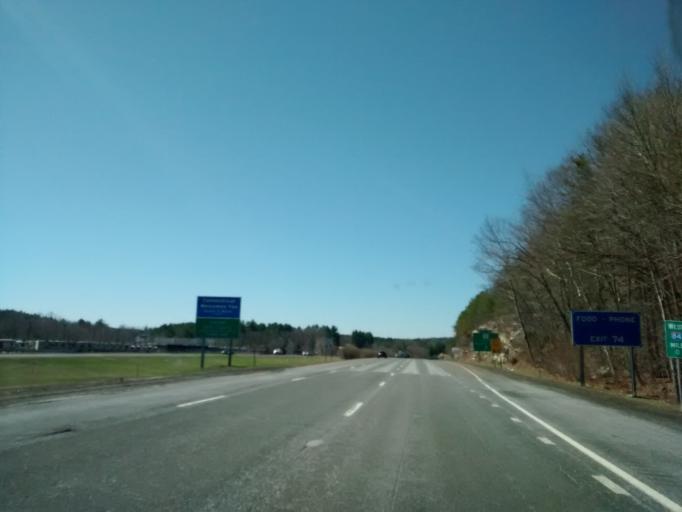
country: US
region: Massachusetts
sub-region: Hampden County
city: Holland
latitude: 42.0307
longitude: -72.1364
